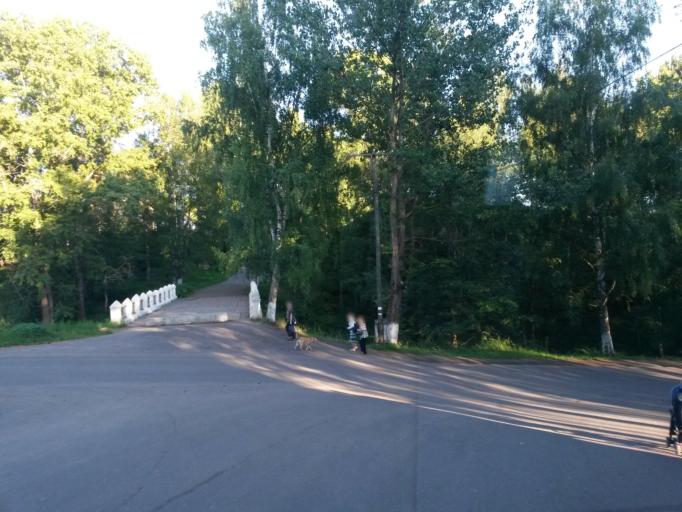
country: RU
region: Jaroslavl
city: Tutayev
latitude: 57.8801
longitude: 39.5454
